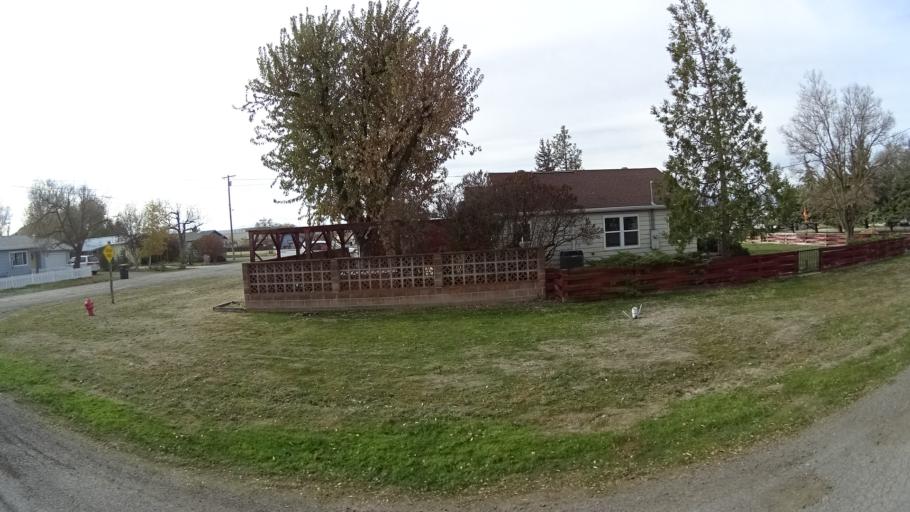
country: US
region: California
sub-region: Siskiyou County
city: Montague
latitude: 41.7264
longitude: -122.5342
